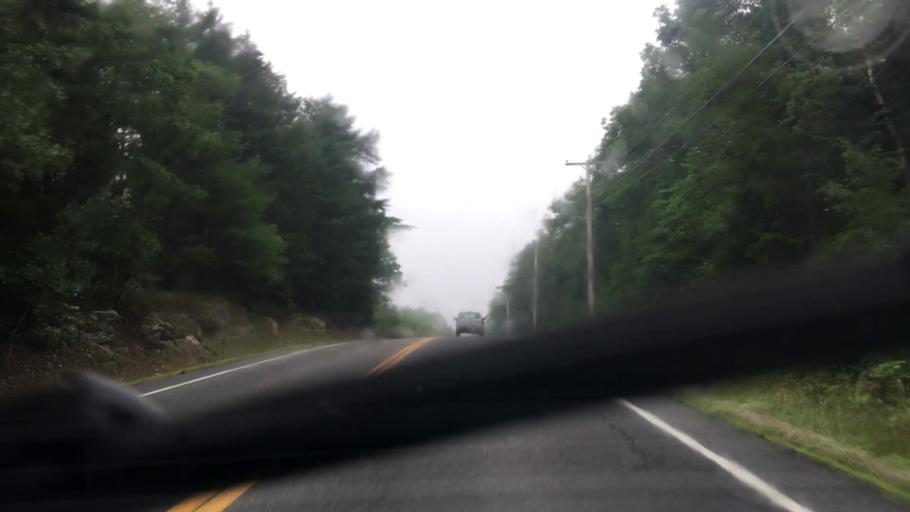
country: US
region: Maine
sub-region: Lincoln County
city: Wiscasset
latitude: 43.9878
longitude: -69.6405
